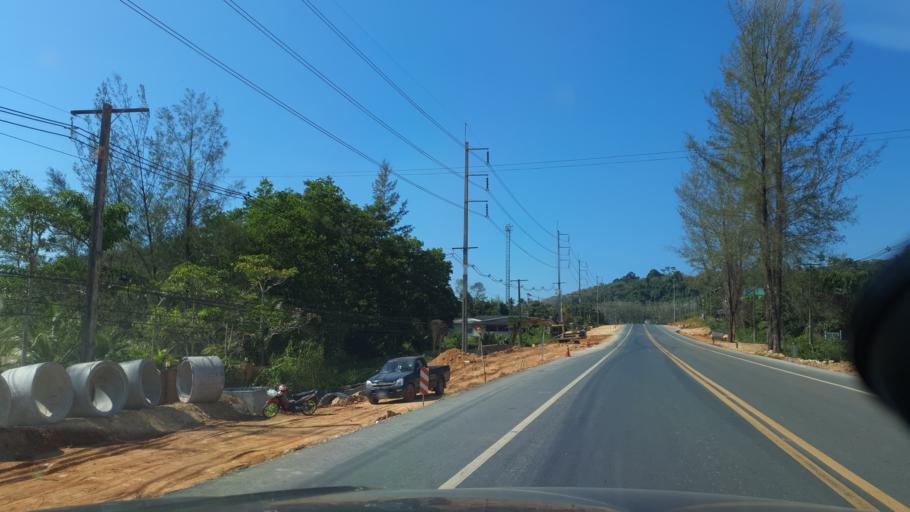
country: TH
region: Phangnga
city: Ban Khao Lak
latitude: 8.6032
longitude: 98.2521
